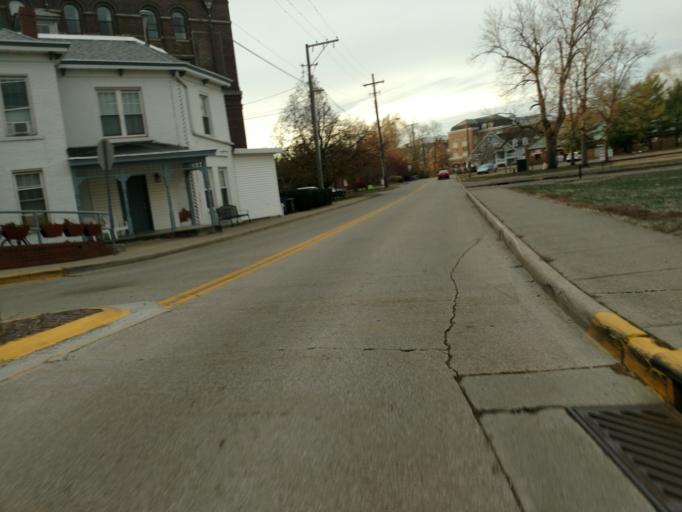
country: US
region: Ohio
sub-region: Athens County
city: Athens
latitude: 39.3291
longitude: -82.1054
